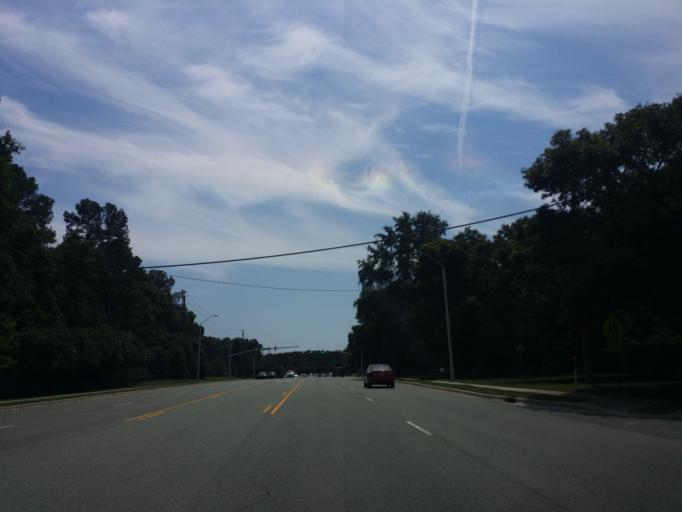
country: US
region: North Carolina
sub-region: Wake County
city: Cary
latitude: 35.8240
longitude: -78.7707
